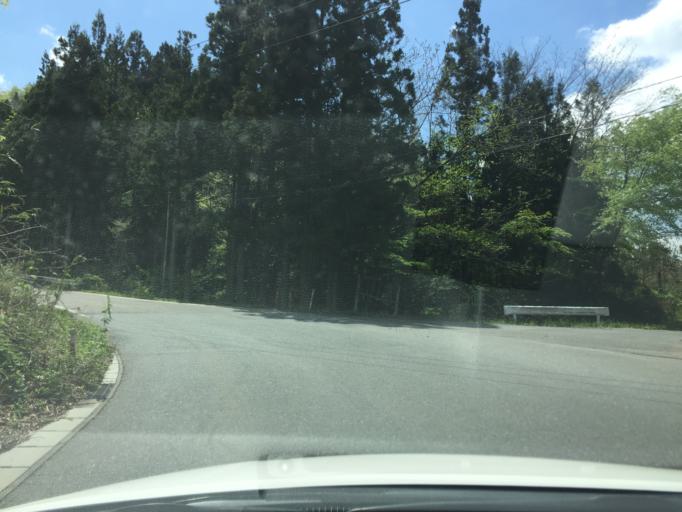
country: JP
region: Fukushima
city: Hobaramachi
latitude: 37.7216
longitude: 140.6433
